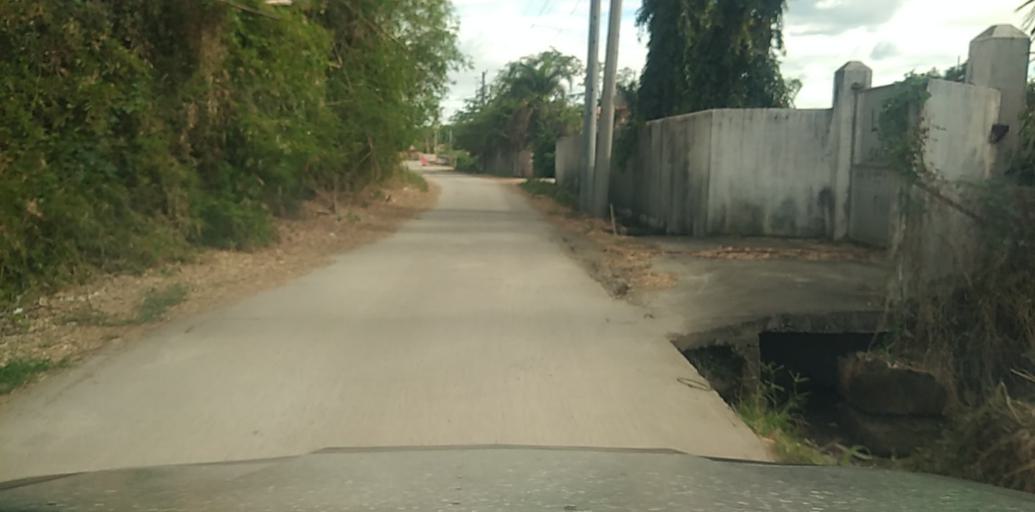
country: PH
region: Central Luzon
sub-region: Province of Pampanga
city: Panlinlang
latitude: 15.1834
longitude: 120.6969
